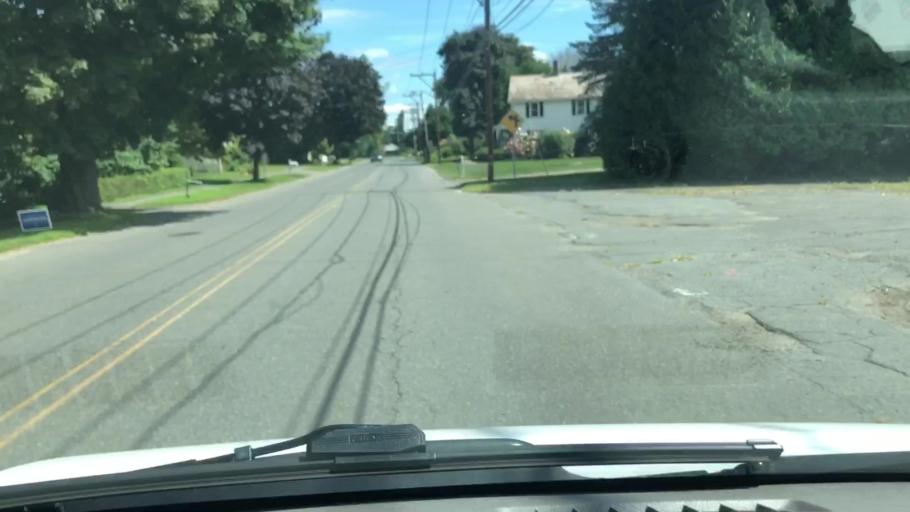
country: US
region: Massachusetts
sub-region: Hampshire County
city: Hatfield
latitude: 42.3660
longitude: -72.6010
